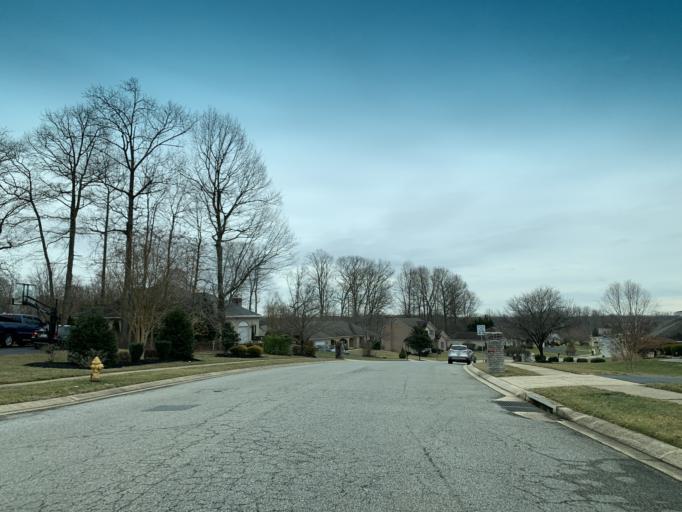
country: US
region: Maryland
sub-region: Harford County
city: Bel Air South
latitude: 39.5016
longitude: -76.2929
